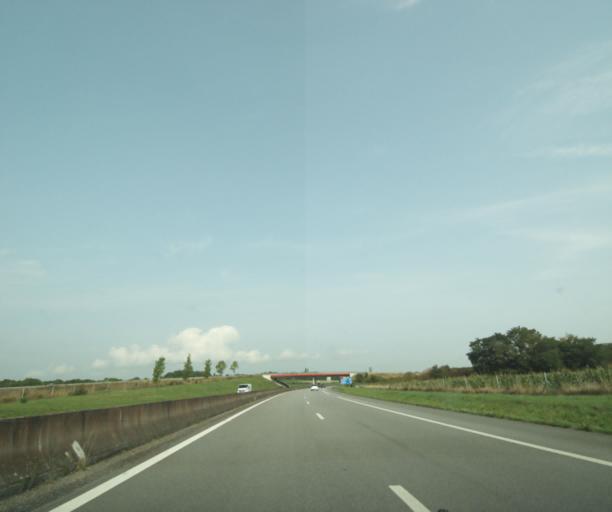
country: FR
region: Lower Normandy
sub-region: Departement de l'Orne
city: Valframbert
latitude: 48.4585
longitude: 0.1264
